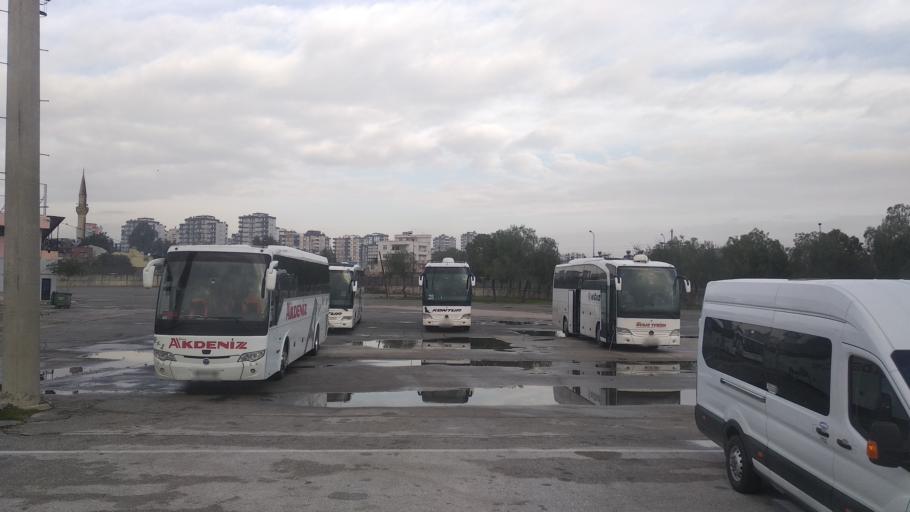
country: TR
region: Adana
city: Seyhan
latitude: 36.9974
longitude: 35.2616
